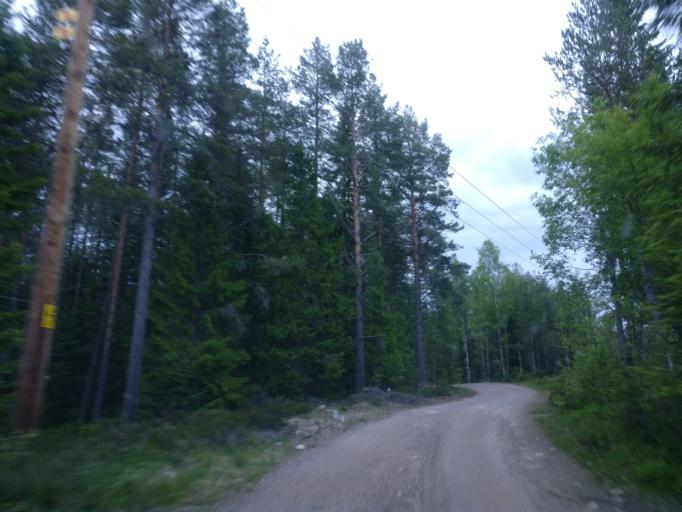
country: SE
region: Vaesternorrland
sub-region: Sundsvalls Kommun
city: Njurundabommen
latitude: 62.2092
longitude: 17.3541
